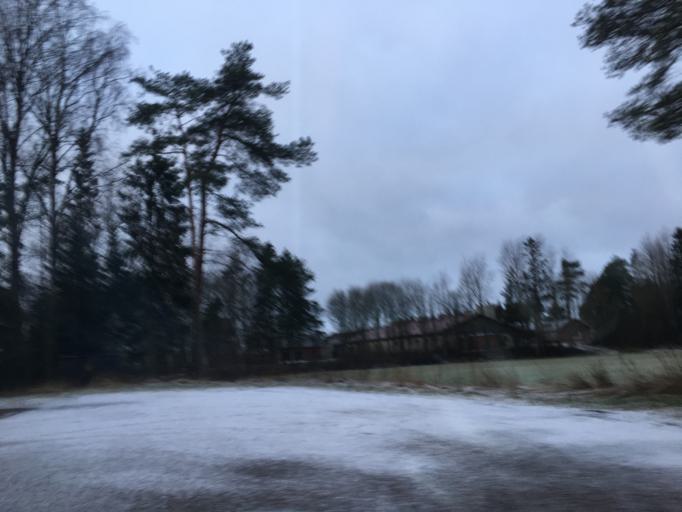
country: FI
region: Varsinais-Suomi
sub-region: Loimaa
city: Aura
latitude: 60.6095
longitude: 22.5617
